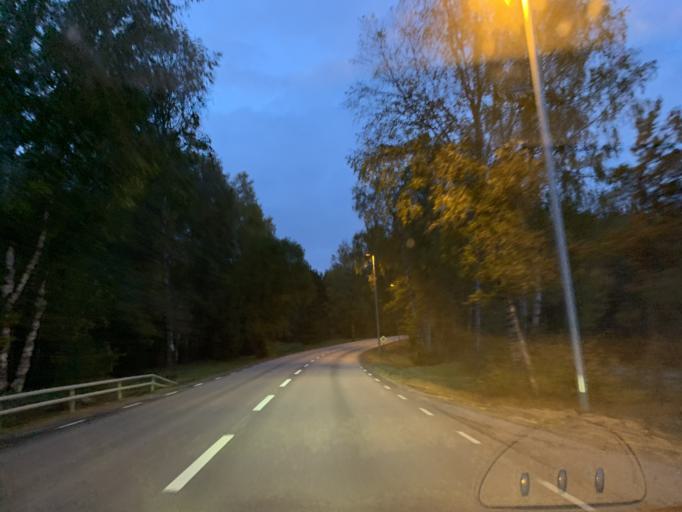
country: SE
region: Stockholm
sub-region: Botkyrka Kommun
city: Varsta
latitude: 59.1710
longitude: 17.7980
